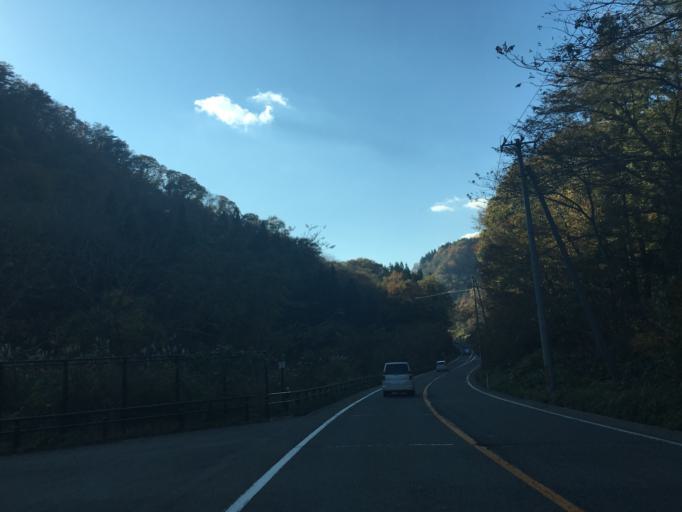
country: JP
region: Fukushima
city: Kitakata
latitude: 37.5760
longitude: 139.6968
